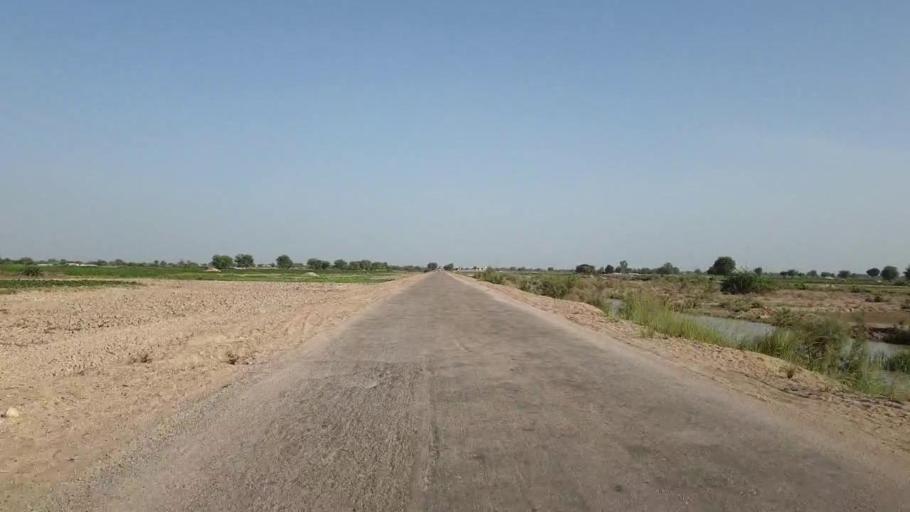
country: PK
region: Sindh
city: Nawabshah
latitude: 26.1473
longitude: 68.4493
